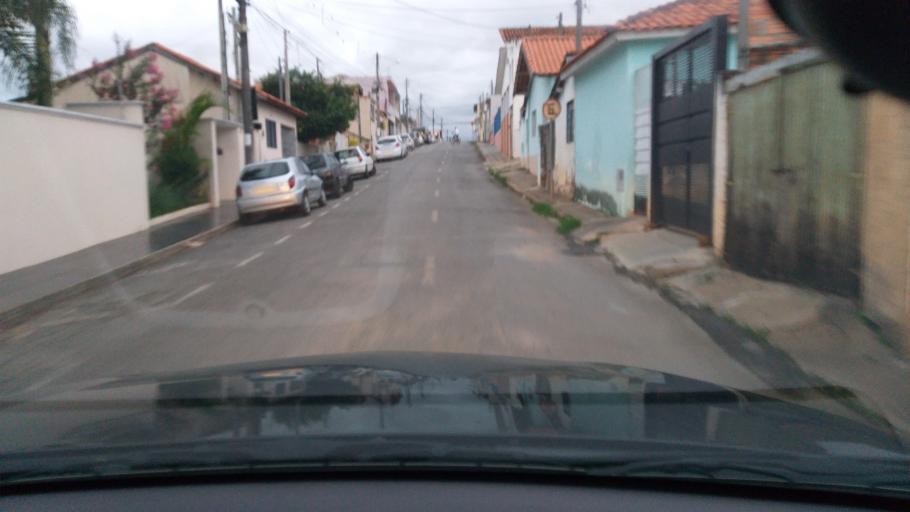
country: BR
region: Sao Paulo
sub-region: Itapeva
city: Itapeva
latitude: -23.9857
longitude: -48.8726
